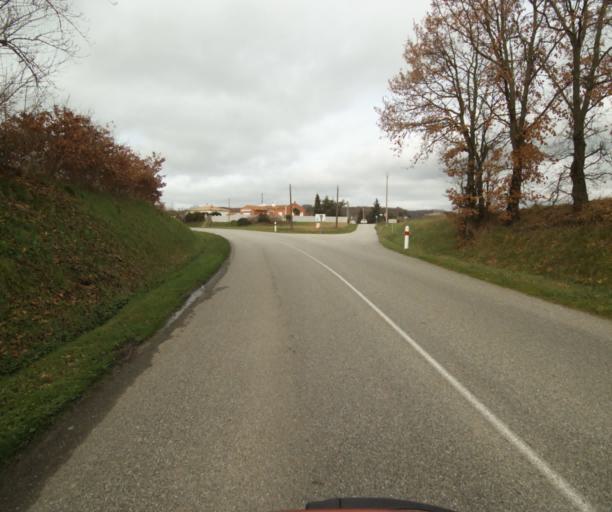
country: FR
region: Midi-Pyrenees
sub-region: Departement de l'Ariege
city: Pamiers
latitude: 43.1496
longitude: 1.5898
